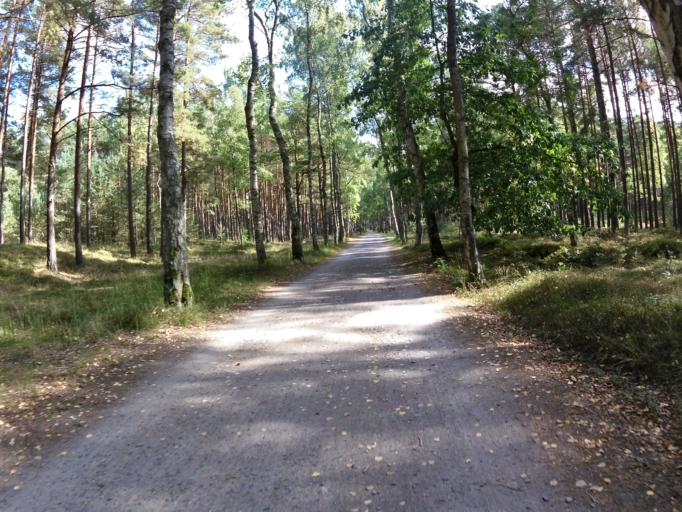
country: DE
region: Mecklenburg-Vorpommern
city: Karlshagen
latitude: 54.0966
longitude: 13.8670
